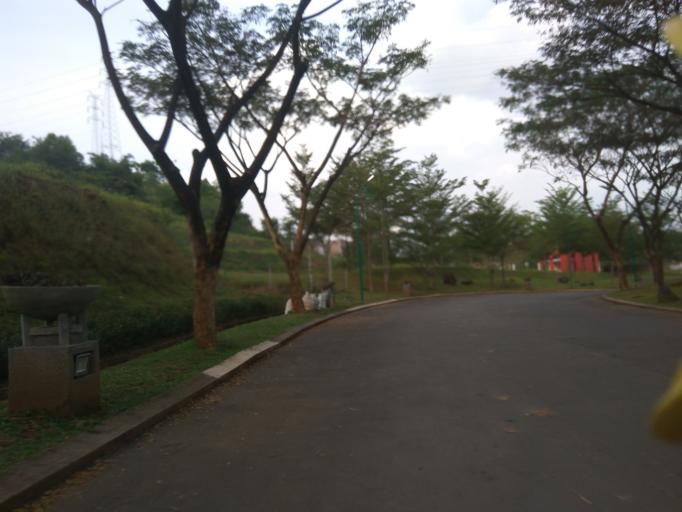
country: ID
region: Central Java
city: Semarang
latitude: -7.0357
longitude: 110.4377
